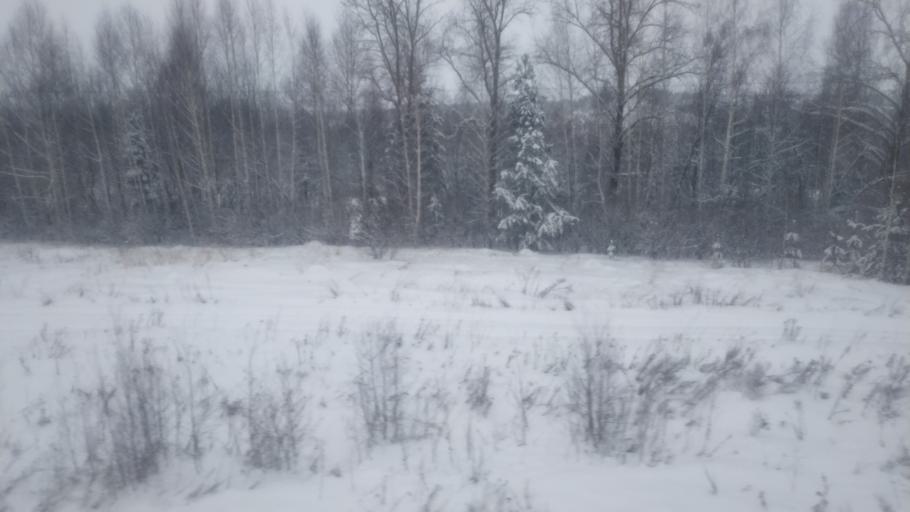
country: RU
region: Udmurtiya
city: Kiyasovo
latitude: 56.5015
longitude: 53.3727
